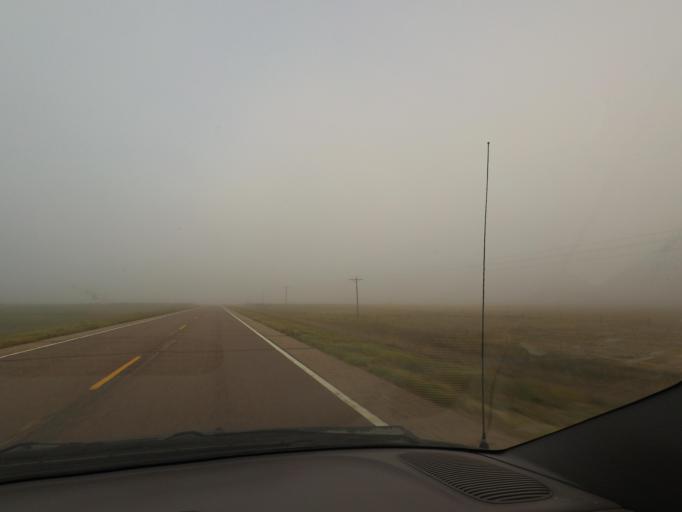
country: US
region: Colorado
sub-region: Kit Carson County
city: Burlington
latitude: 39.6581
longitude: -102.5412
